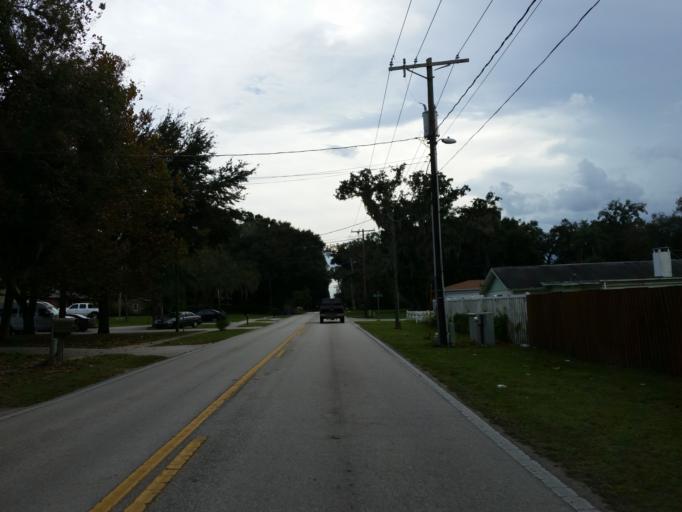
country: US
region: Florida
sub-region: Hillsborough County
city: Brandon
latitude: 27.9298
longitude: -82.2776
